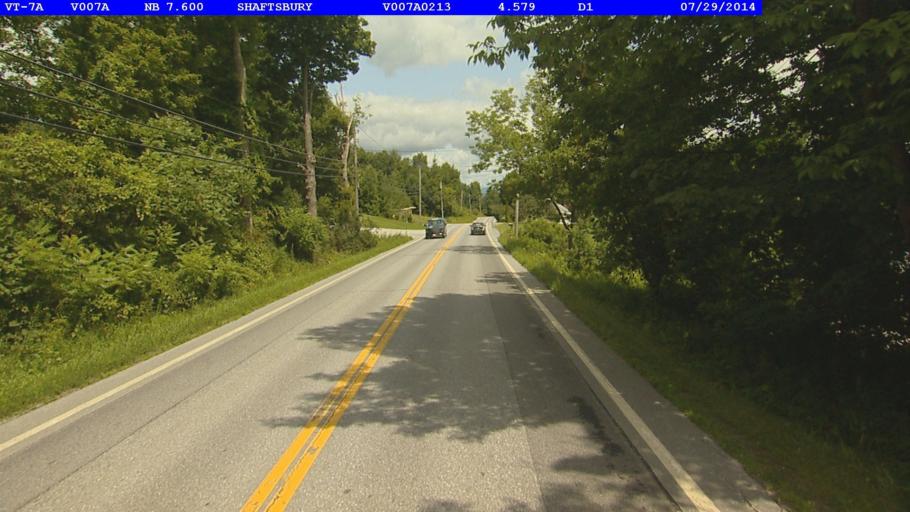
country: US
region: Vermont
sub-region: Bennington County
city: North Bennington
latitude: 42.9974
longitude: -73.2011
